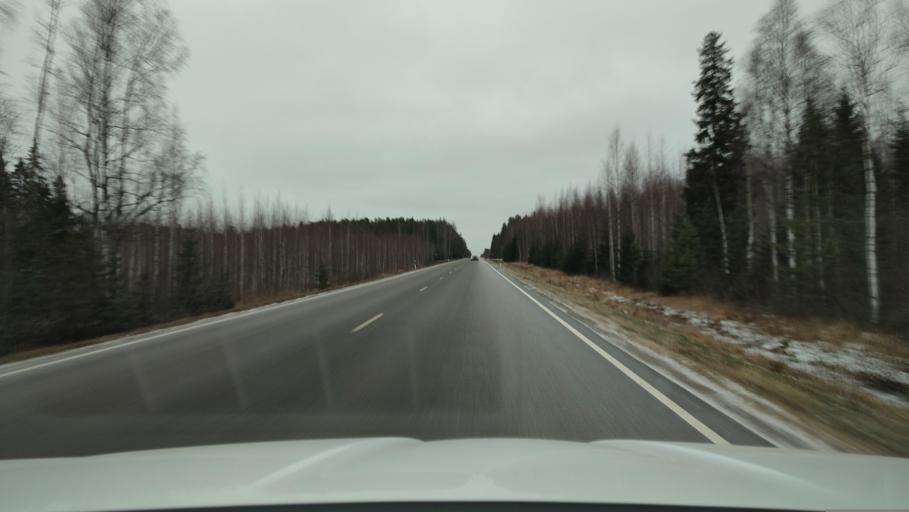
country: FI
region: Ostrobothnia
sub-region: Sydosterbotten
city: Naerpes
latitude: 62.5669
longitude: 21.4841
